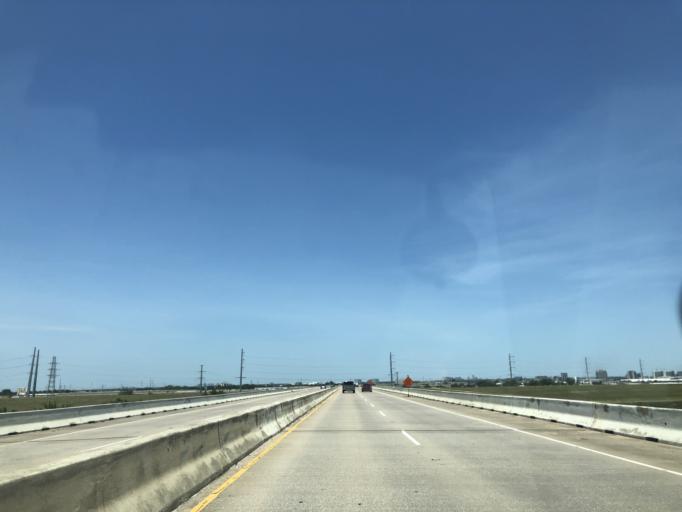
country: US
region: Texas
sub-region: Dallas County
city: Irving
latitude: 32.8047
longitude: -96.9044
